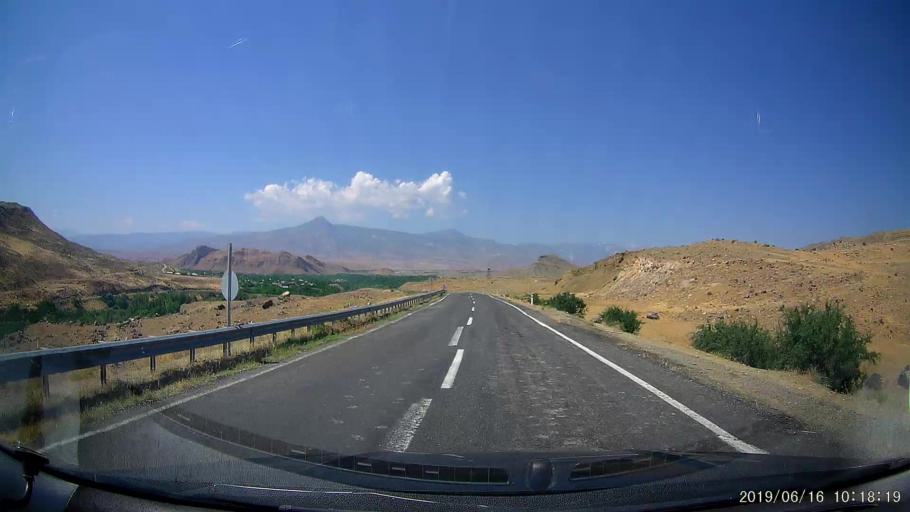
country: TR
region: Igdir
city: Tuzluca
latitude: 40.1616
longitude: 43.6697
